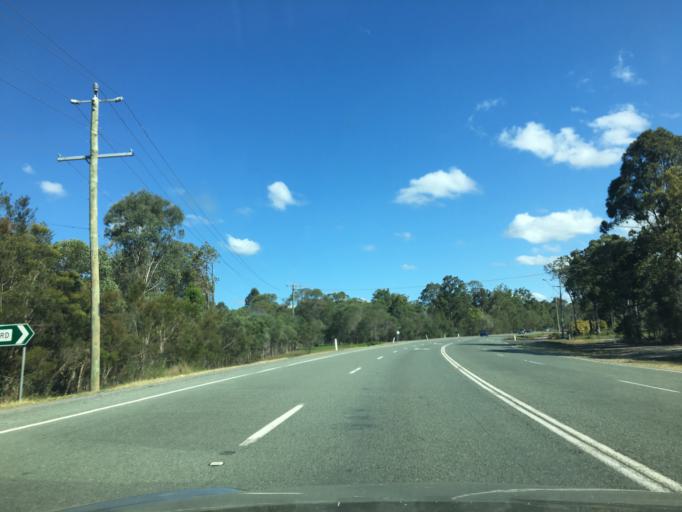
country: AU
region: Queensland
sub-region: Logan
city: Logan Reserve
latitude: -27.7303
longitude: 153.1286
